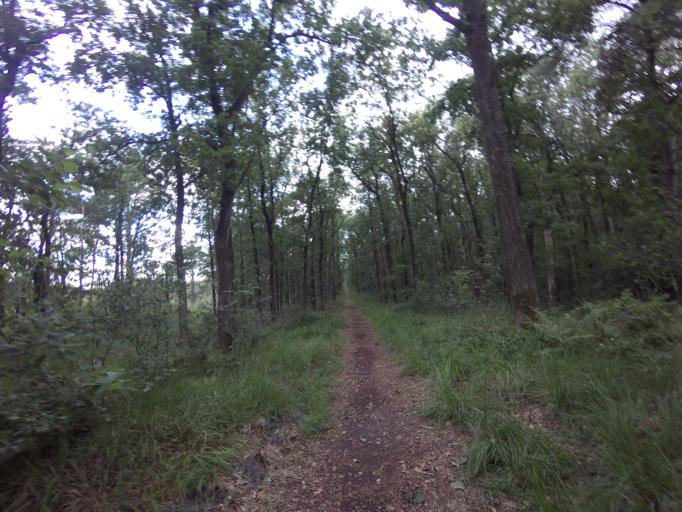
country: NL
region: Friesland
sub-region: Gemeente Heerenveen
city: Jubbega
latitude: 52.9632
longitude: 6.1749
